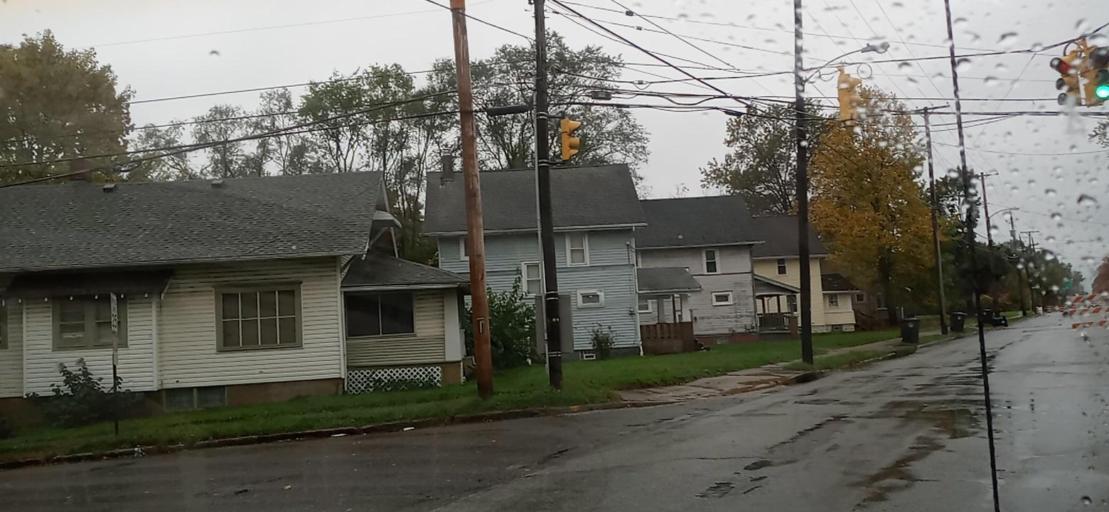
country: US
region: Ohio
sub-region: Summit County
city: Akron
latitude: 41.0616
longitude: -81.5562
